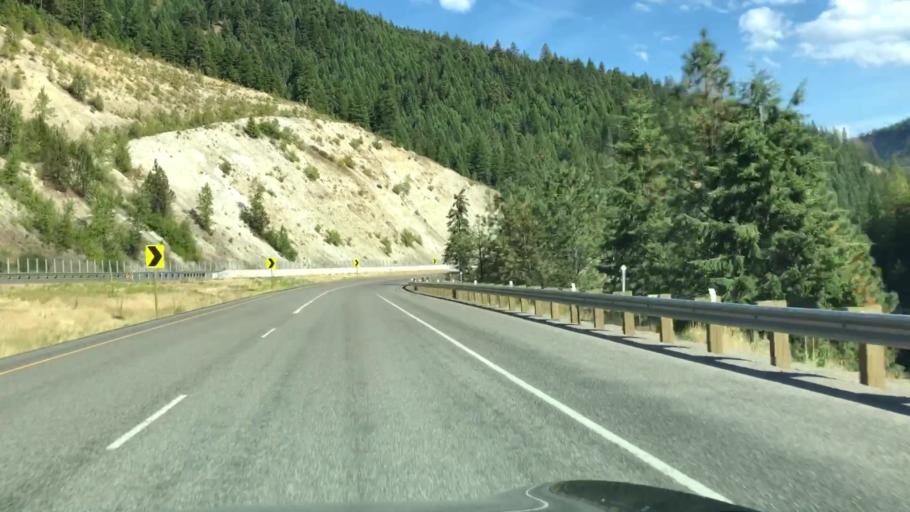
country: US
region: Montana
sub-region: Sanders County
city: Thompson Falls
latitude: 47.3122
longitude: -115.2129
